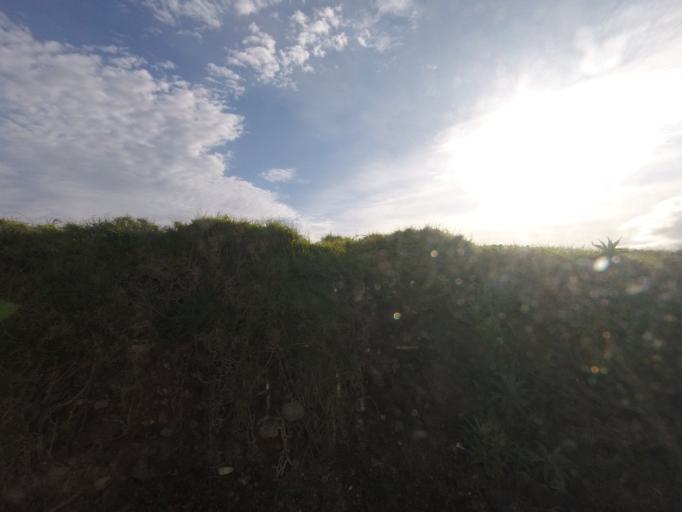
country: PT
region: Madeira
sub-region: Machico
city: Canical
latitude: 32.7484
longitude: -16.7407
